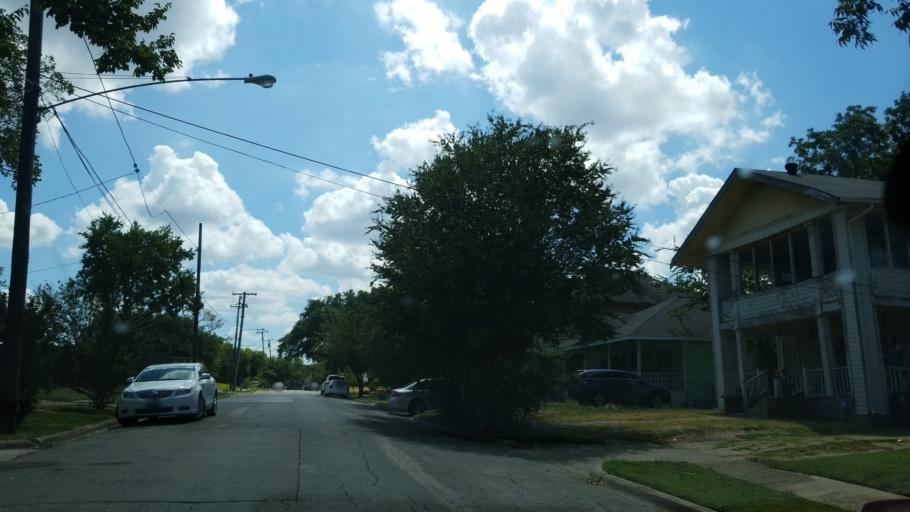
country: US
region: Texas
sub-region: Dallas County
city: Dallas
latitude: 32.7532
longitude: -96.8253
